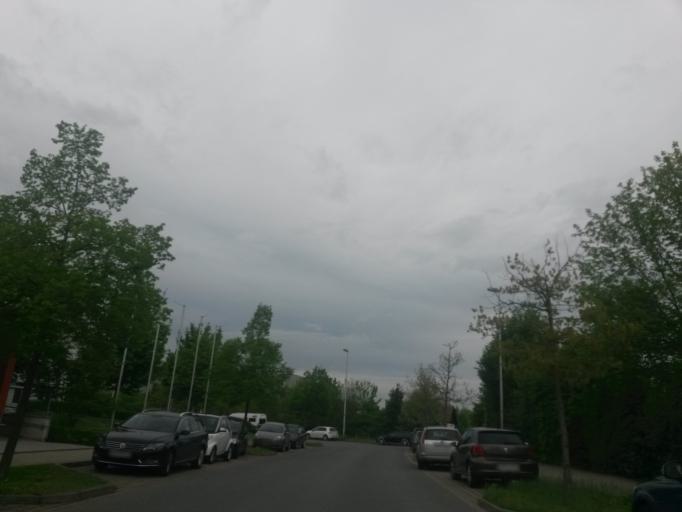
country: DE
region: Bavaria
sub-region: Regierungsbezirk Mittelfranken
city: Erlangen
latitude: 49.5475
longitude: 11.0202
